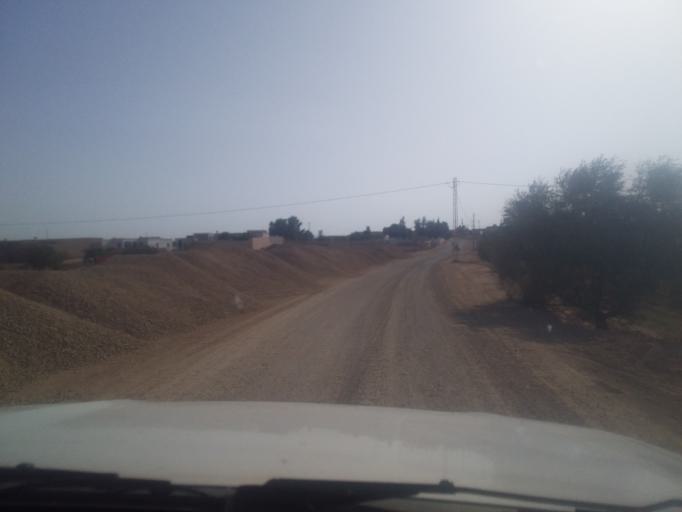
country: TN
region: Qabis
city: Matmata
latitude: 33.5859
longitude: 10.2690
